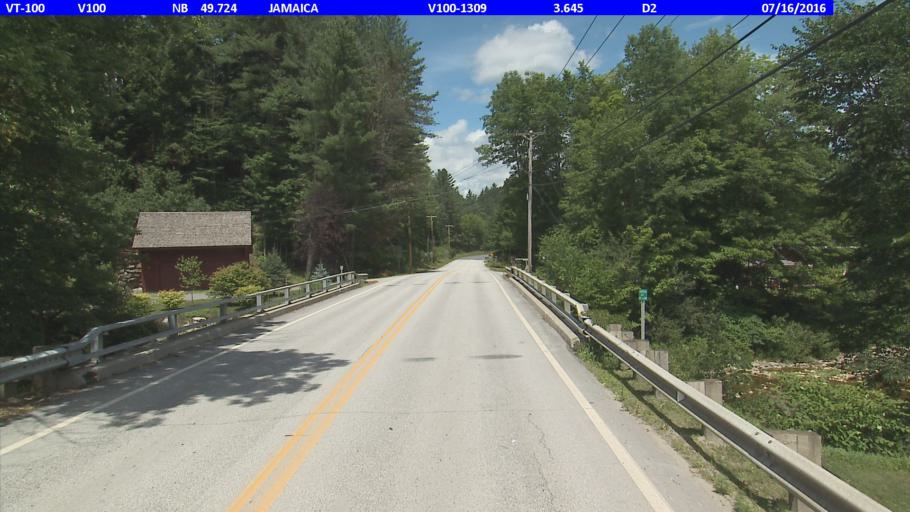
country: US
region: Vermont
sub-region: Windham County
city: Dover
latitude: 43.1470
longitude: -72.8412
